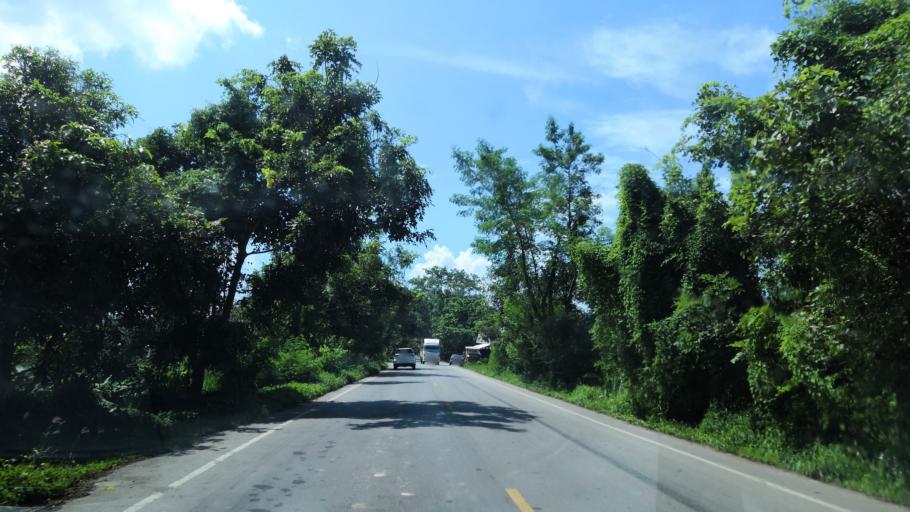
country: TH
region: Chiang Rai
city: Wiang Chai
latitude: 19.9611
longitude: 99.9556
